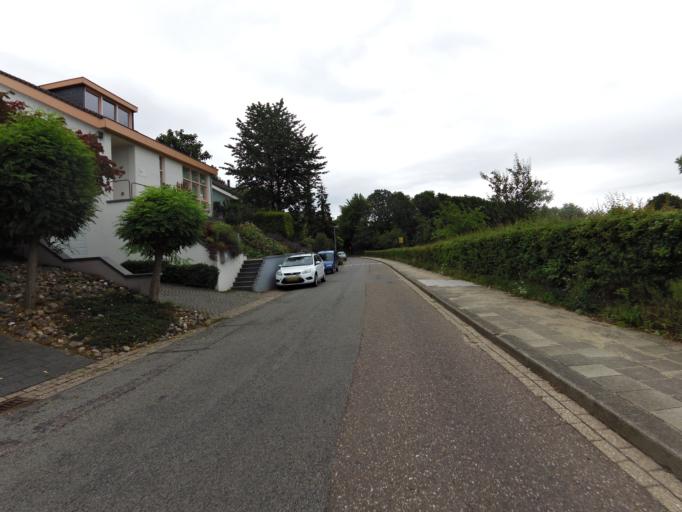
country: NL
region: Limburg
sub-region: Gemeente Voerendaal
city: Klimmen
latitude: 50.8740
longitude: 5.8772
